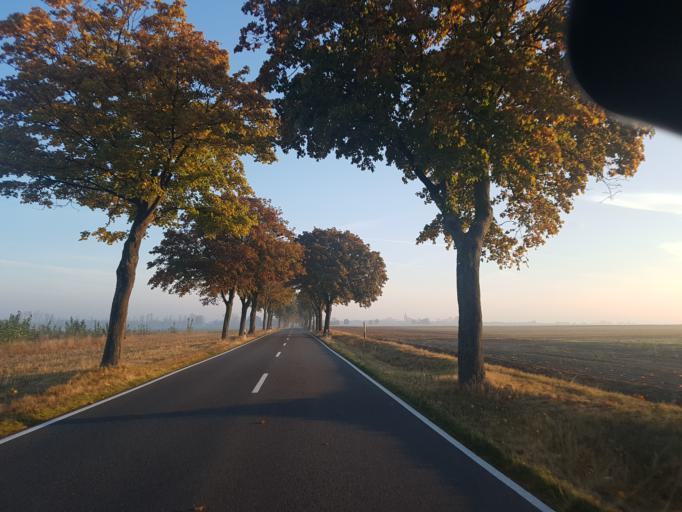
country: DE
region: Brandenburg
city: Juterbog
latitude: 51.9093
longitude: 13.0798
